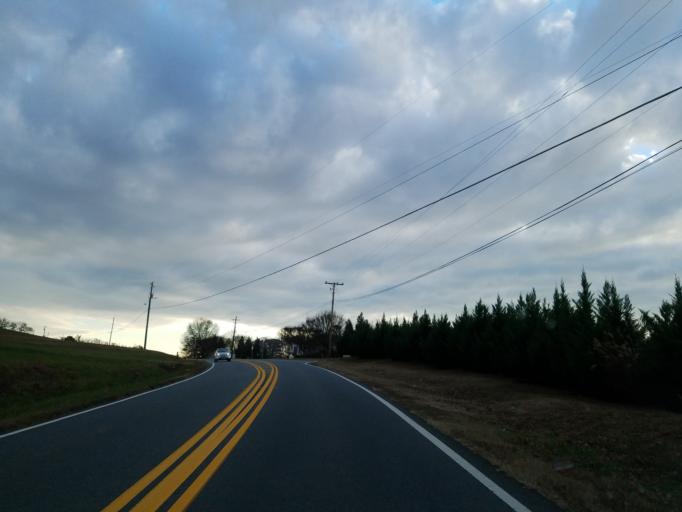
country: US
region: Georgia
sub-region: Forsyth County
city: Cumming
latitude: 34.2933
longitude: -84.0876
